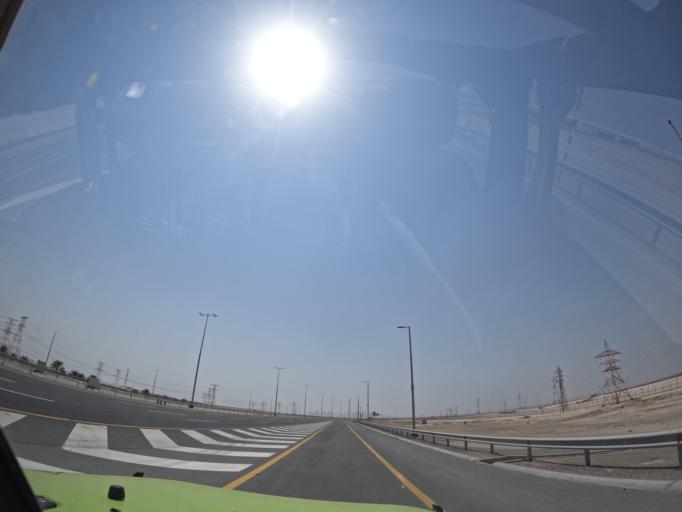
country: AE
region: Abu Dhabi
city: Abu Dhabi
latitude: 24.1631
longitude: 54.3536
